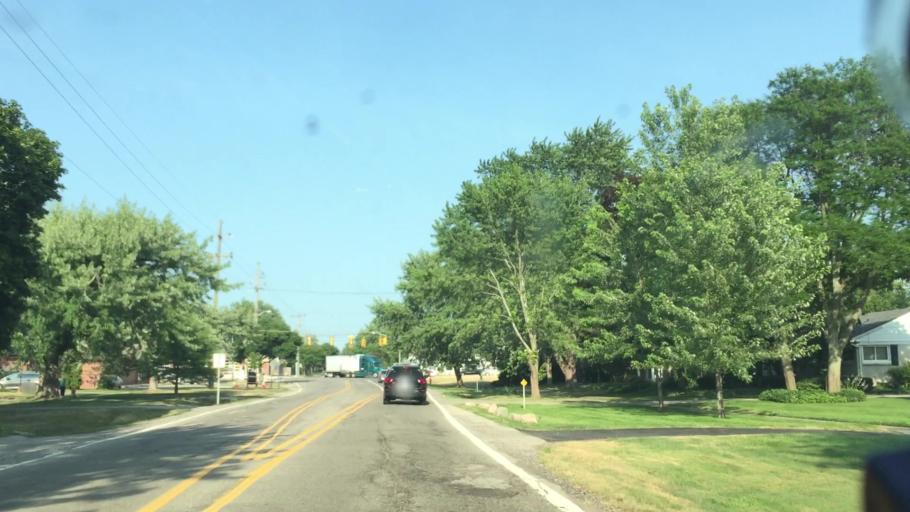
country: US
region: Michigan
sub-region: Oakland County
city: Beverly Hills
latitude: 42.5313
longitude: -83.2260
